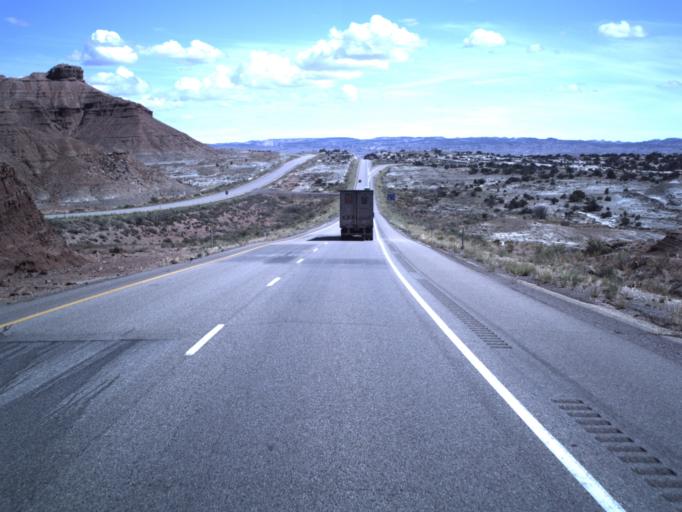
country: US
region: Utah
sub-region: Emery County
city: Ferron
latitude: 38.8314
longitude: -111.1318
